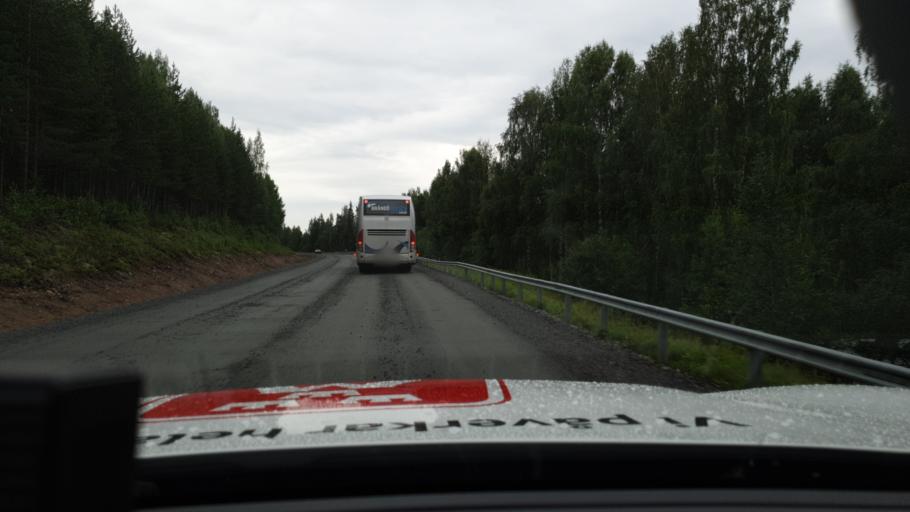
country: SE
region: Norrbotten
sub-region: Alvsbyns Kommun
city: AElvsbyn
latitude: 66.1492
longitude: 20.8747
